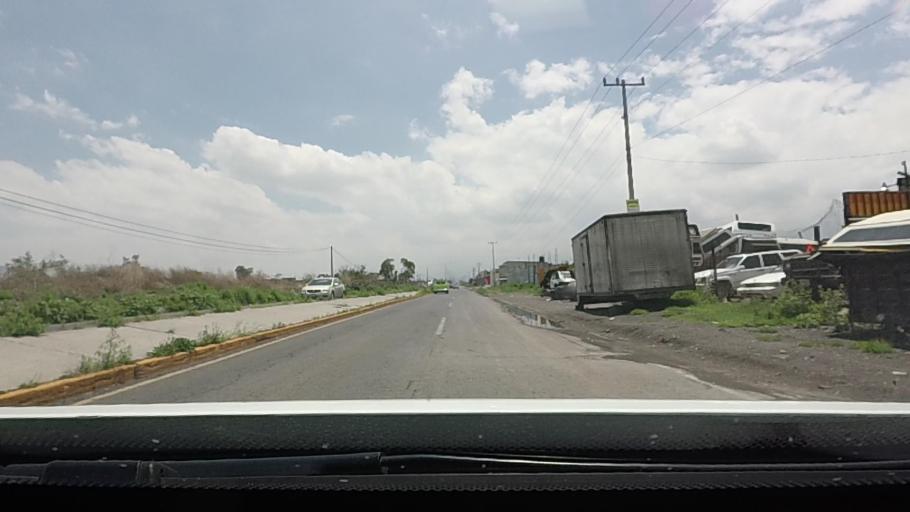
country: MX
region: Mexico
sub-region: Chalco
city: Barrio de Guadalupe
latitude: 19.2502
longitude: -98.9190
